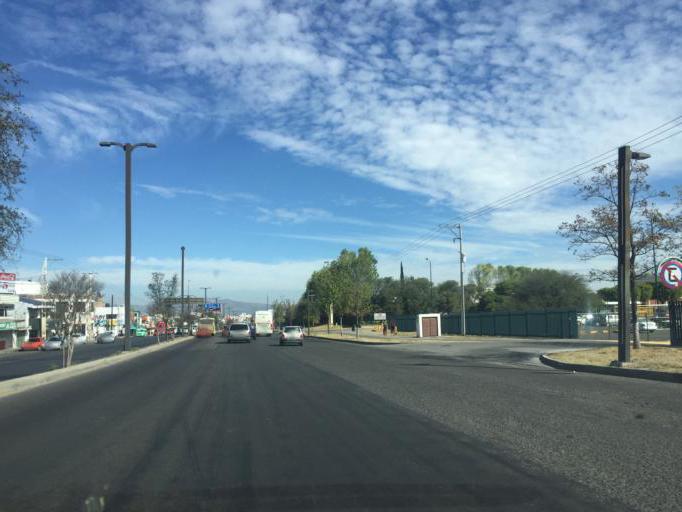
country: MX
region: Queretaro
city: San Juan del Rio
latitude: 20.3785
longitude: -99.9857
